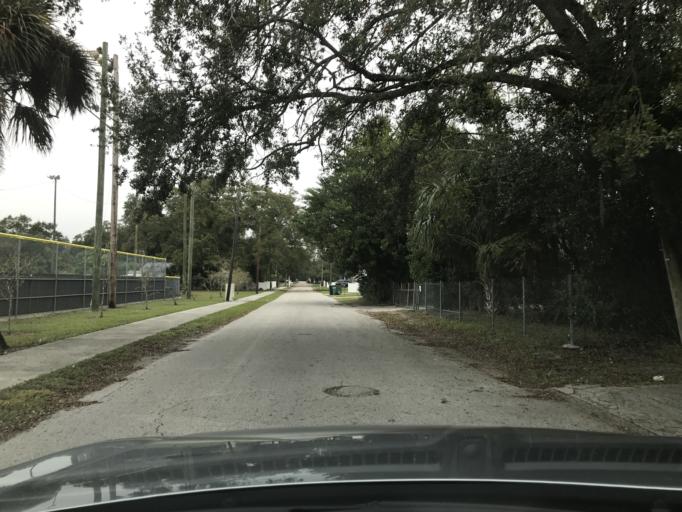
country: US
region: Florida
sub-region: Hillsborough County
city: Tampa
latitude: 27.9780
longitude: -82.4646
